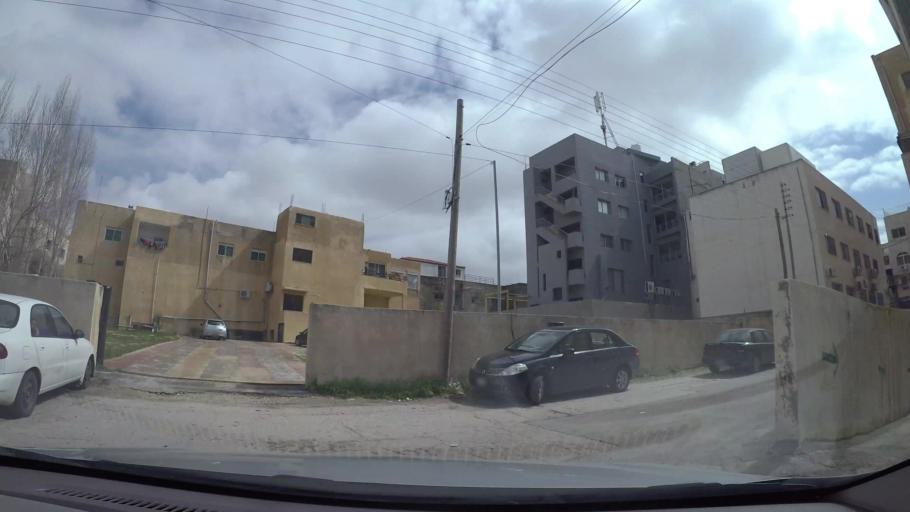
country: JO
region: Amman
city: Al Jubayhah
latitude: 31.9907
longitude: 35.8484
